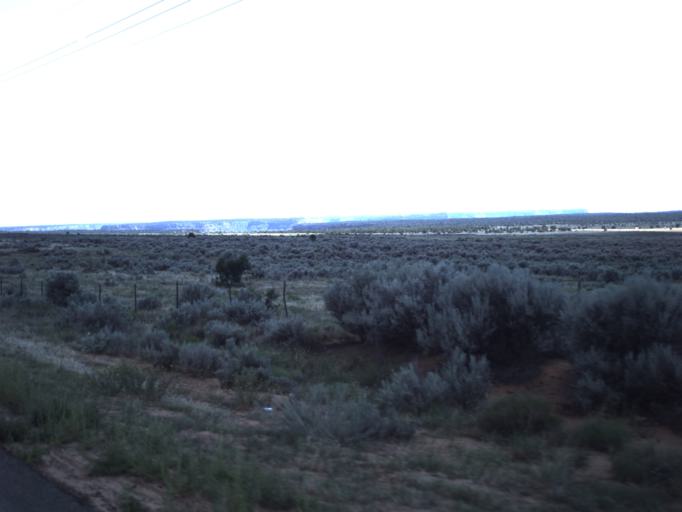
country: US
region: Arizona
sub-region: Mohave County
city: Colorado City
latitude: 37.0612
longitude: -113.0993
